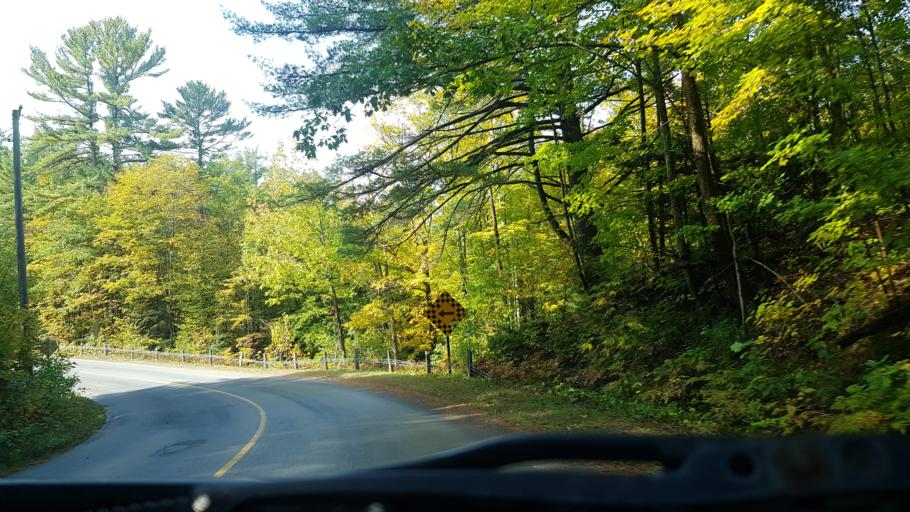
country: CA
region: Ontario
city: Gravenhurst
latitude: 44.7887
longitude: -79.2315
